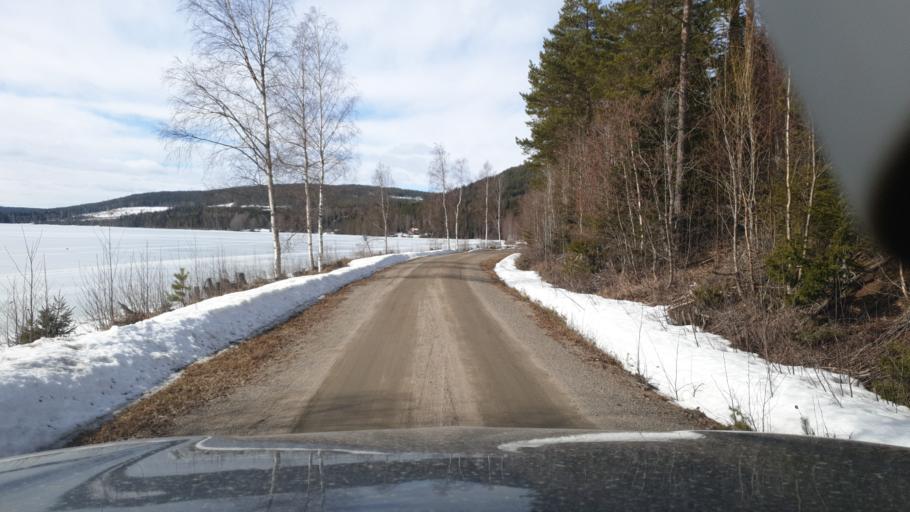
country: SE
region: Gaevleborg
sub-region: Ljusdals Kommun
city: Farila
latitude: 61.8466
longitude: 15.9205
